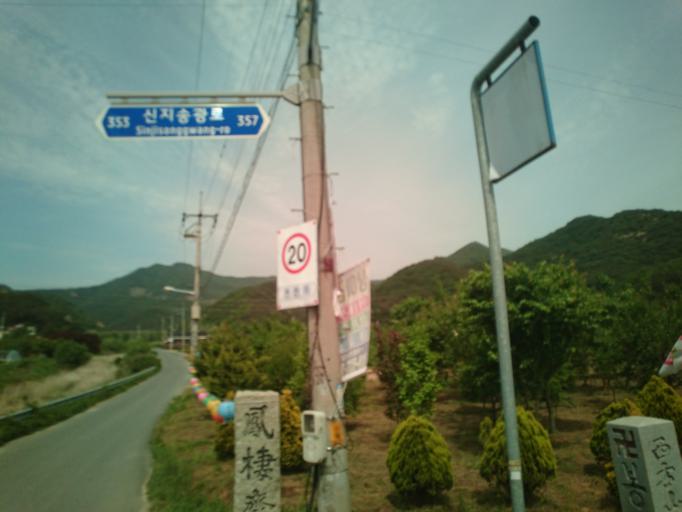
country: KR
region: Jeollabuk-do
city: Wanju
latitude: 35.8971
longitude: 127.1912
